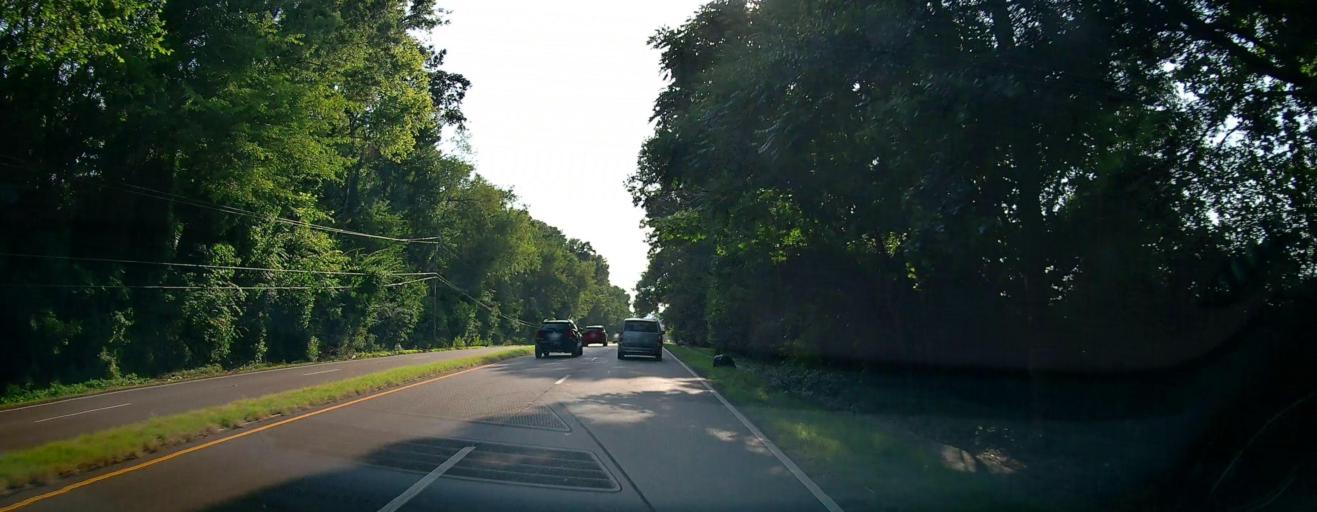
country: US
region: Alabama
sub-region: Jefferson County
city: Mountain Brook
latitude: 33.5276
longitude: -86.7540
